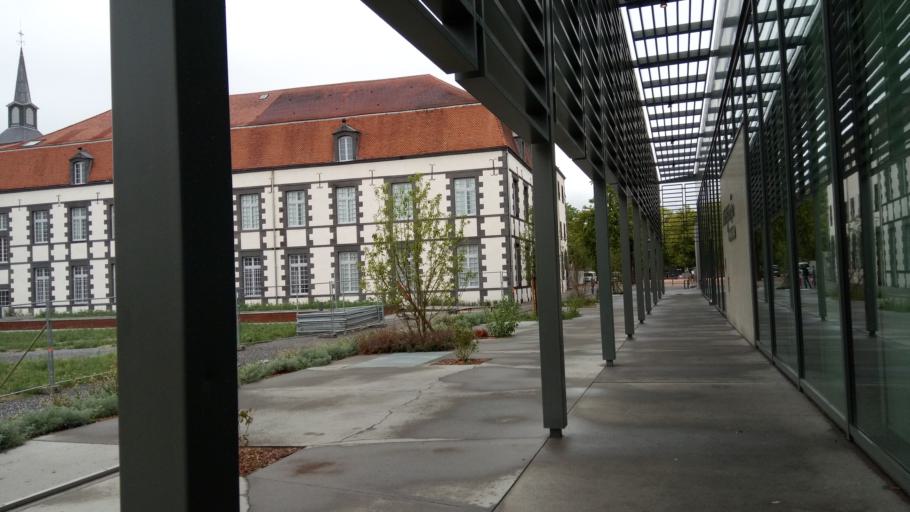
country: FR
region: Auvergne
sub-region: Departement du Puy-de-Dome
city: Riom
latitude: 45.8953
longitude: 3.1202
